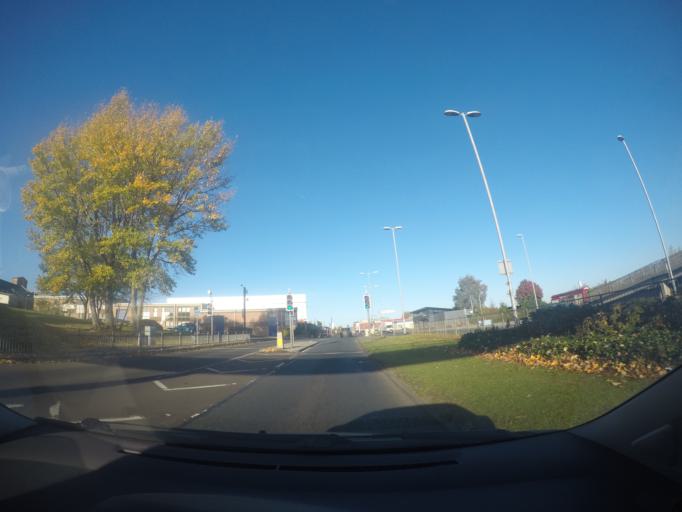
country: GB
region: England
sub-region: City and Borough of Leeds
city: Leeds
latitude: 53.7974
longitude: -1.5747
